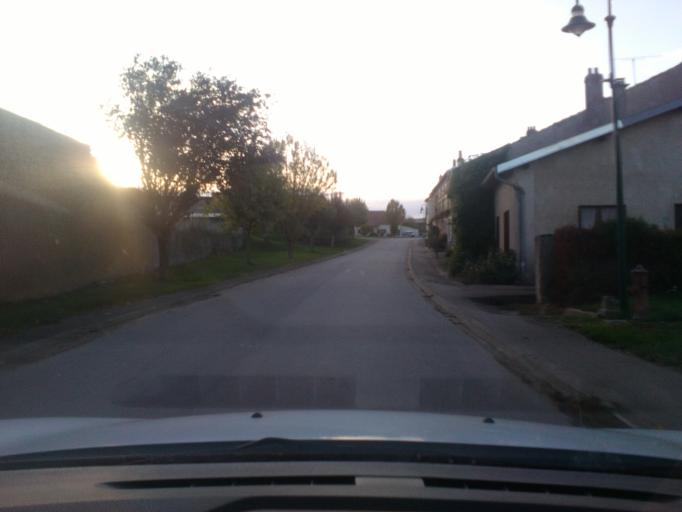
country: FR
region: Lorraine
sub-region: Departement des Vosges
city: Mirecourt
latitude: 48.3991
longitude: 6.1671
